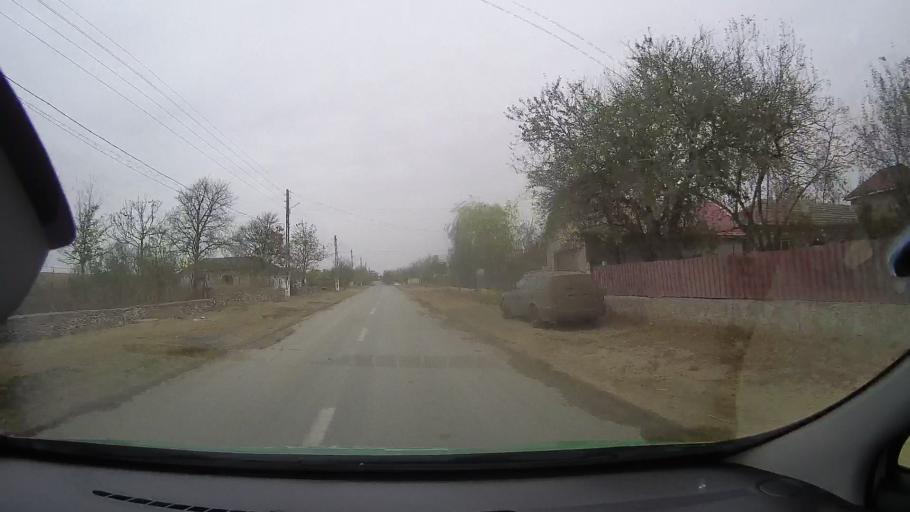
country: RO
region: Constanta
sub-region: Comuna Vulturu
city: Vulturu
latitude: 44.6437
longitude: 28.2722
